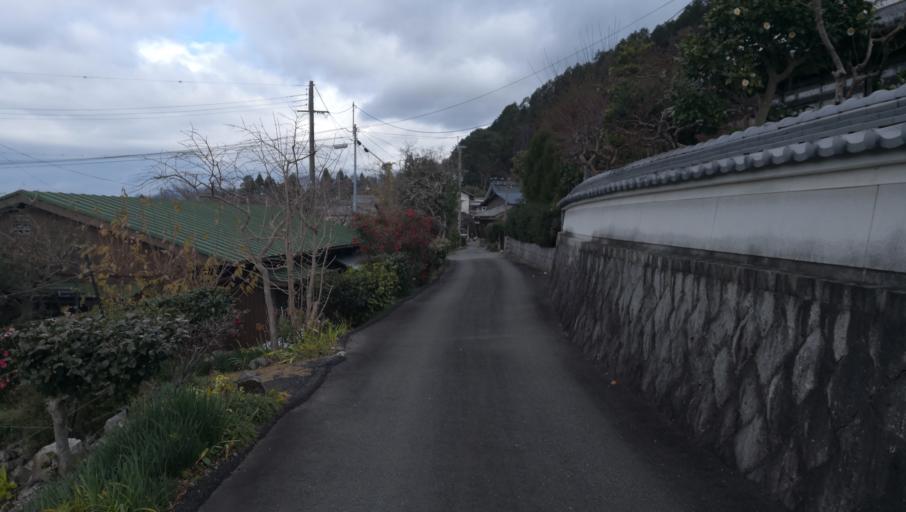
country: JP
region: Kyoto
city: Kameoka
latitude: 35.0343
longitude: 135.5875
